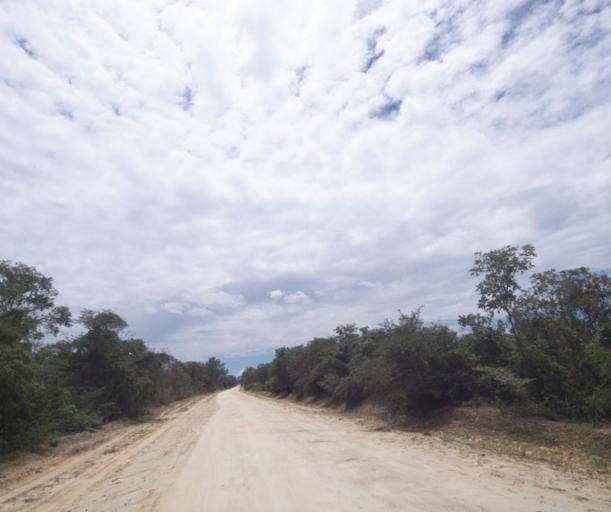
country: BR
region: Bahia
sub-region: Carinhanha
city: Carinhanha
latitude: -14.2099
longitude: -43.9127
